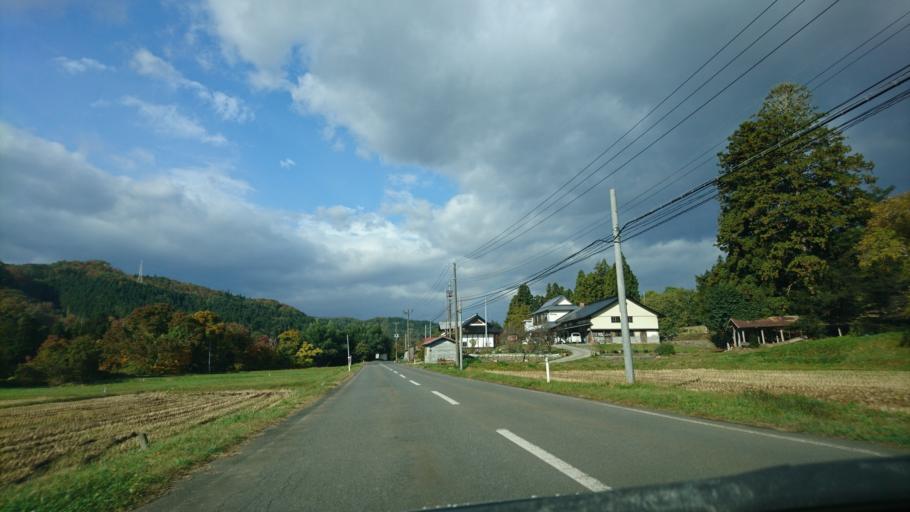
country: JP
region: Iwate
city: Mizusawa
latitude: 39.0735
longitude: 141.0166
